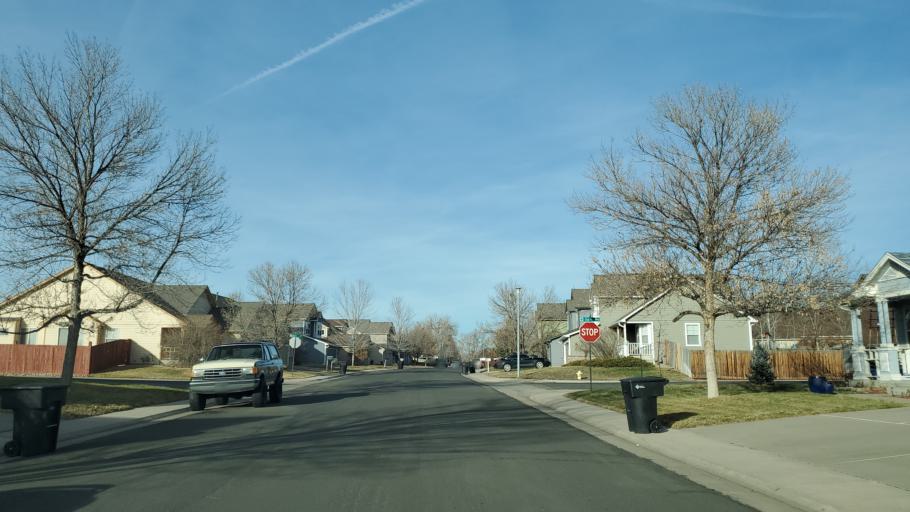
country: US
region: Colorado
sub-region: Adams County
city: Northglenn
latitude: 39.9067
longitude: -104.9583
